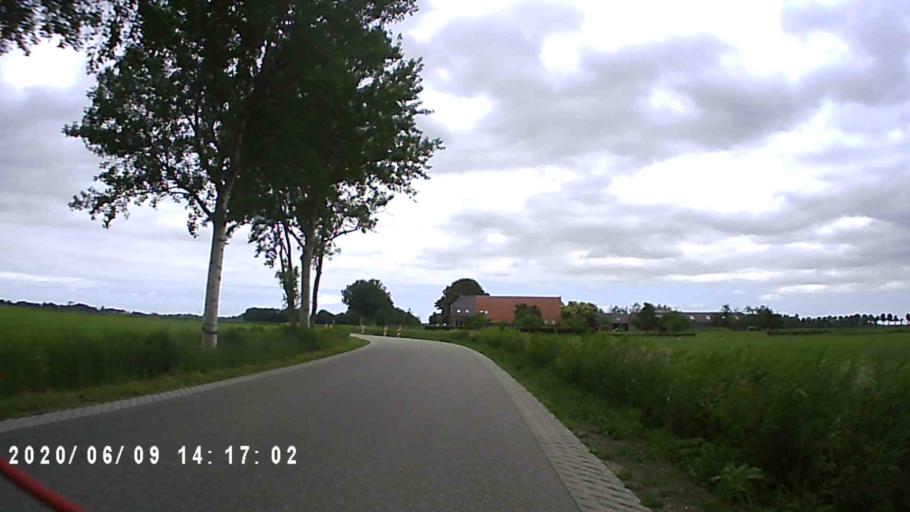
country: NL
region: Groningen
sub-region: Gemeente Bedum
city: Bedum
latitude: 53.2822
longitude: 6.5929
